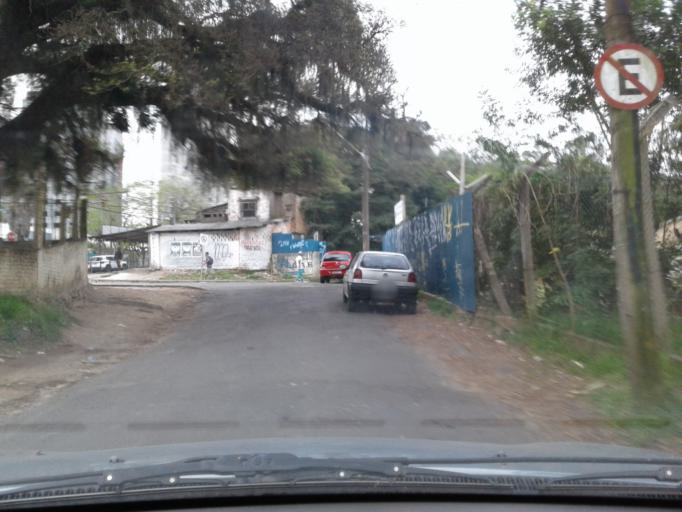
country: BR
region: Rio Grande do Sul
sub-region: Porto Alegre
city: Porto Alegre
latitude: -30.0619
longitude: -51.1484
